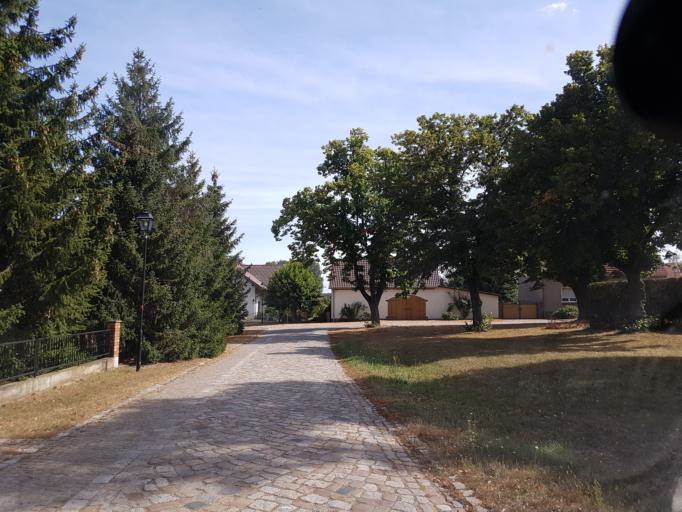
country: DE
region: Brandenburg
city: Drahnsdorf
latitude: 51.8608
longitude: 13.6269
